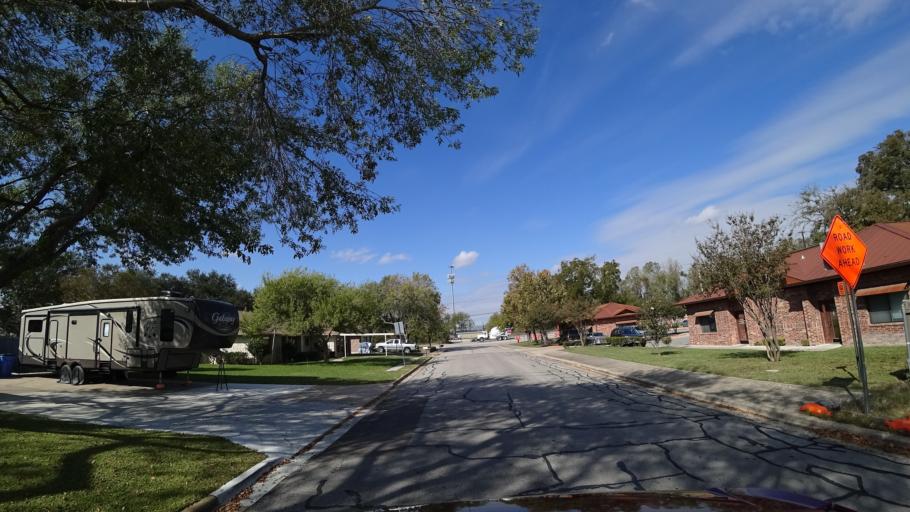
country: US
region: Texas
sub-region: Travis County
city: Windemere
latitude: 30.4595
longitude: -97.6485
